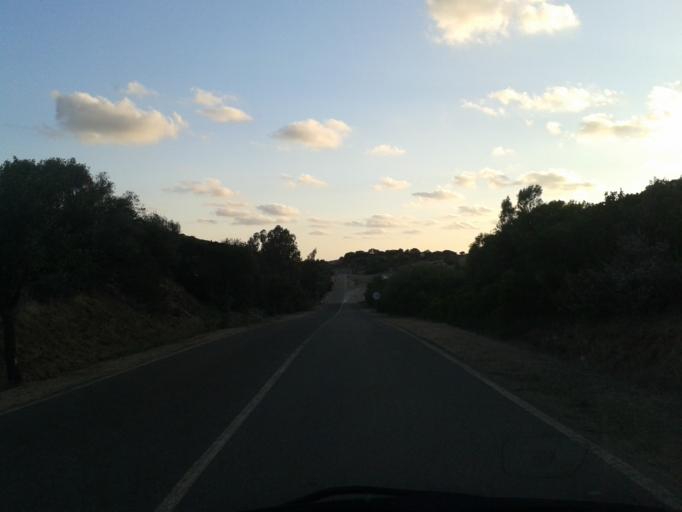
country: IT
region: Sardinia
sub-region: Provincia di Cagliari
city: Villasimius
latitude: 39.1384
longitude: 9.5385
